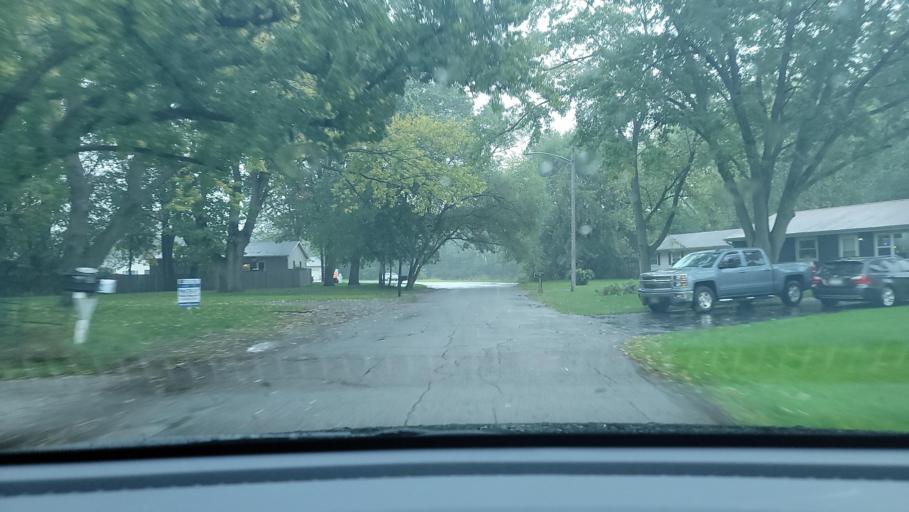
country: US
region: Indiana
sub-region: Porter County
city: Portage
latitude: 41.5903
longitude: -87.1791
